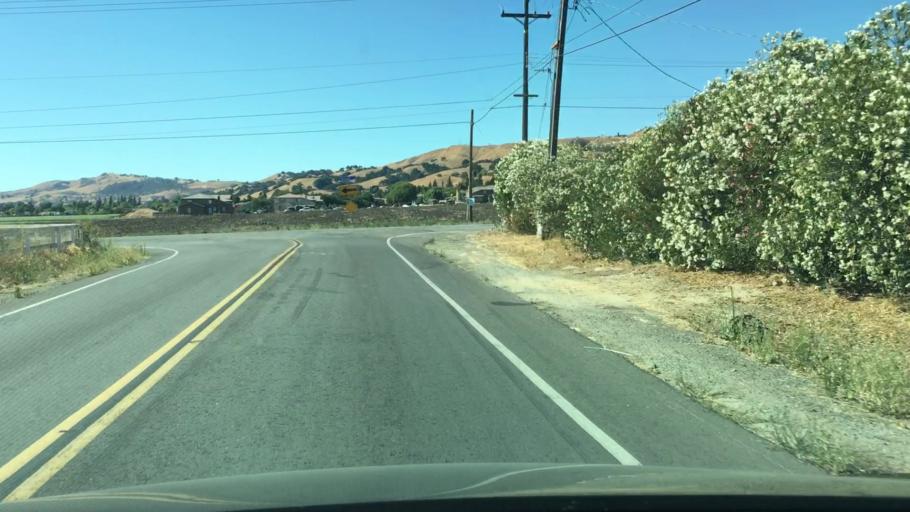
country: US
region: California
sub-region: Santa Clara County
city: San Martin
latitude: 37.1287
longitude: -121.6005
